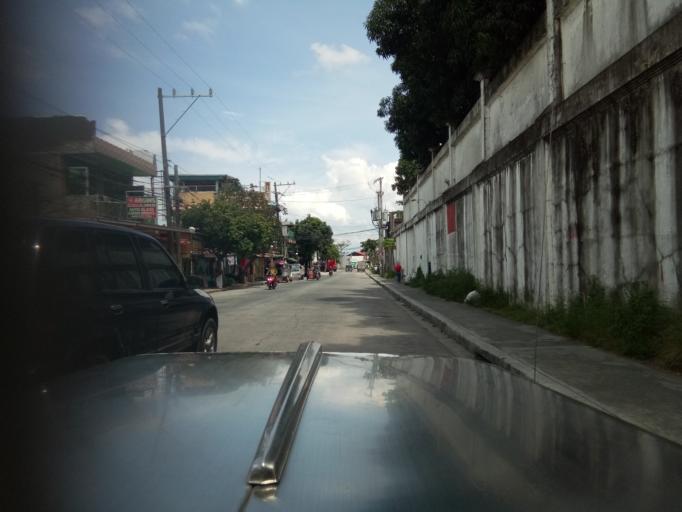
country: PH
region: Calabarzon
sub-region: Province of Cavite
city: Bulihan
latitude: 14.2855
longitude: 120.9972
